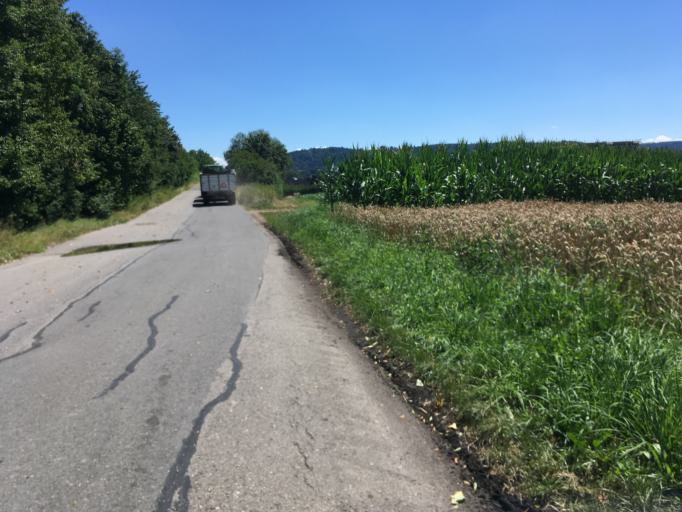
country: CH
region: Vaud
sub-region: Broye-Vully District
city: Avenches
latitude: 46.8927
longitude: 7.0402
